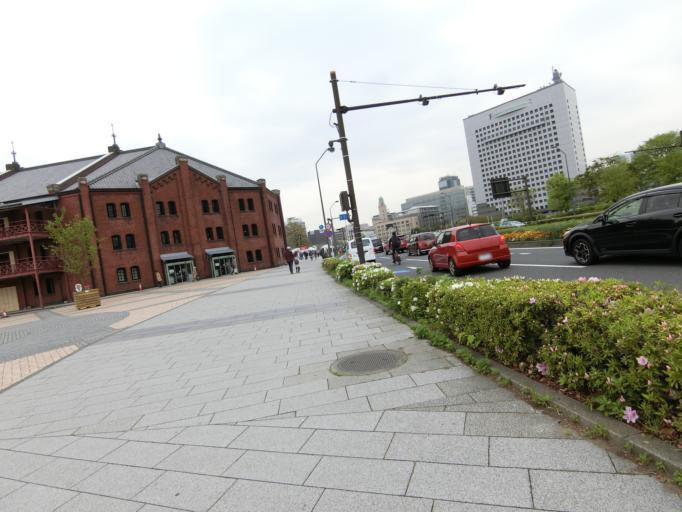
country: JP
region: Kanagawa
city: Yokohama
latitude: 35.4528
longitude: 139.6418
